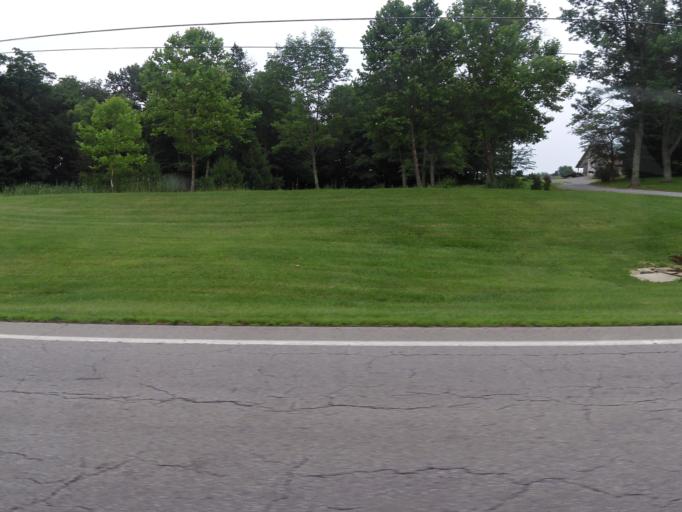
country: US
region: Ohio
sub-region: Clinton County
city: Blanchester
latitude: 39.2529
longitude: -83.9040
